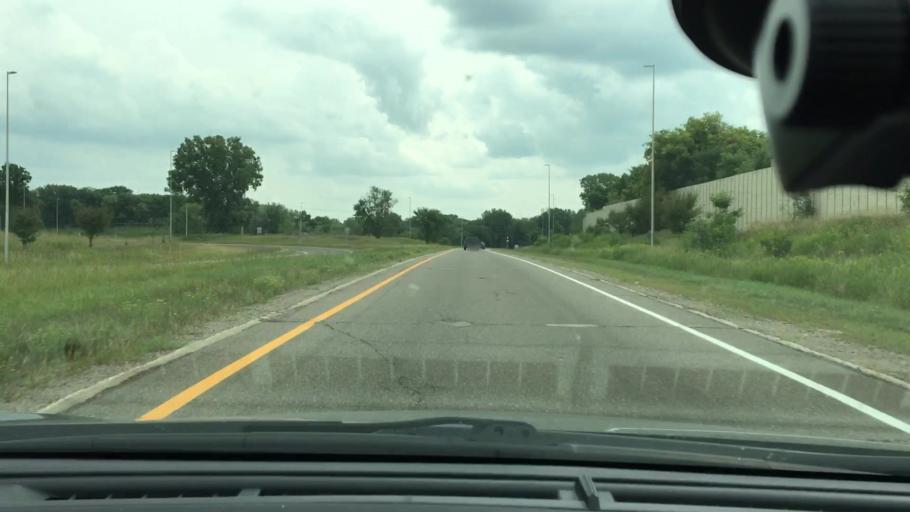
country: US
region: Minnesota
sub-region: Hennepin County
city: Osseo
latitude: 45.0825
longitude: -93.4044
